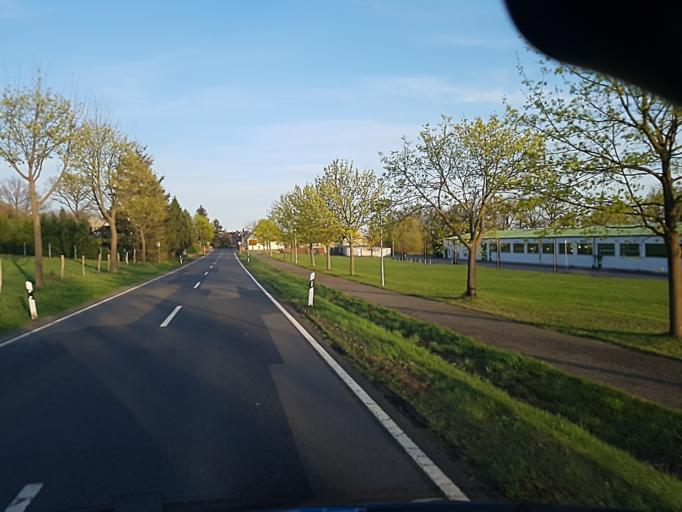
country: DE
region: Saxony
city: Elsnig
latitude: 51.5639
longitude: 12.8756
